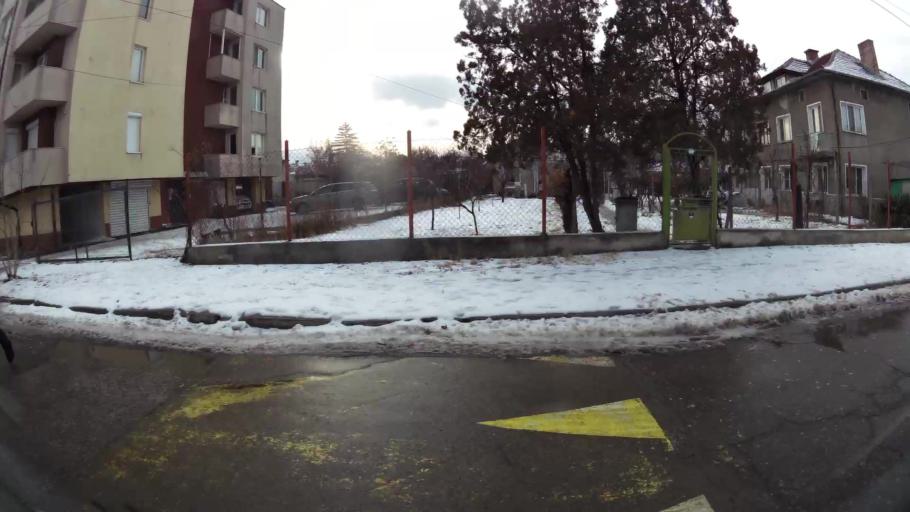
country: BG
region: Sofia-Capital
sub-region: Stolichna Obshtina
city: Sofia
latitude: 42.6970
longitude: 23.3729
